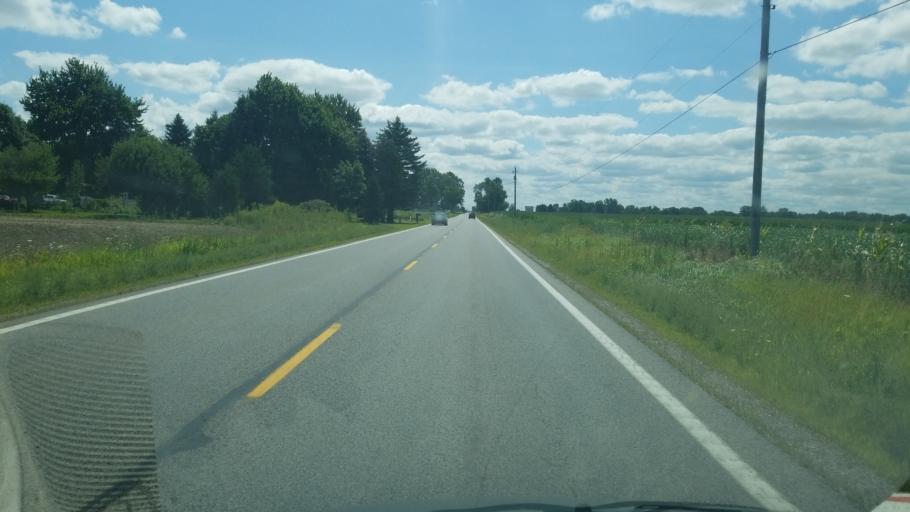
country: US
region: Ohio
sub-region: Fulton County
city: Delta
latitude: 41.6140
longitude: -84.0375
